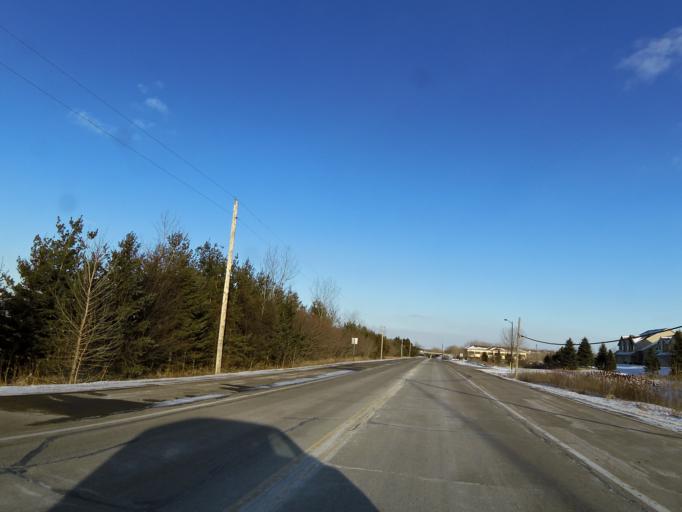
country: US
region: Minnesota
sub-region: Dakota County
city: Lakeville
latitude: 44.6523
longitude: -93.3036
